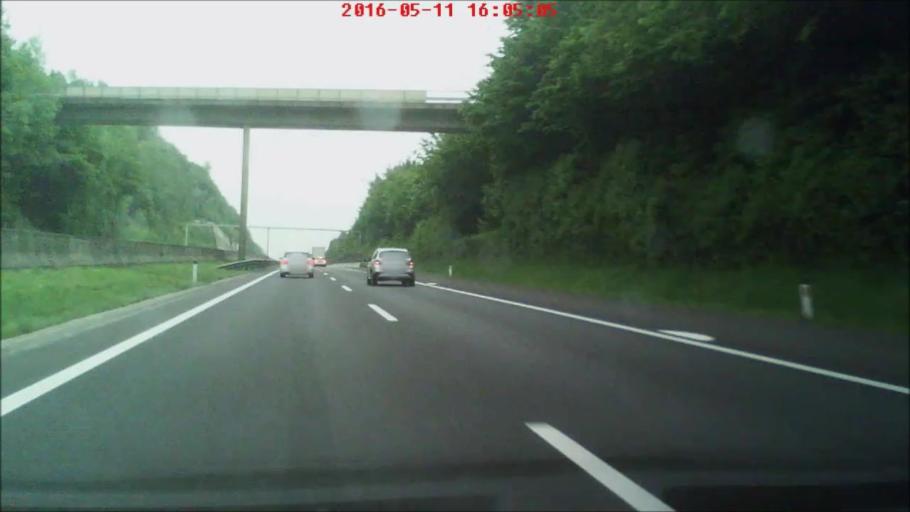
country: AT
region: Styria
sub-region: Politischer Bezirk Leibnitz
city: Weitendorf
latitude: 46.8737
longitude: 15.4839
